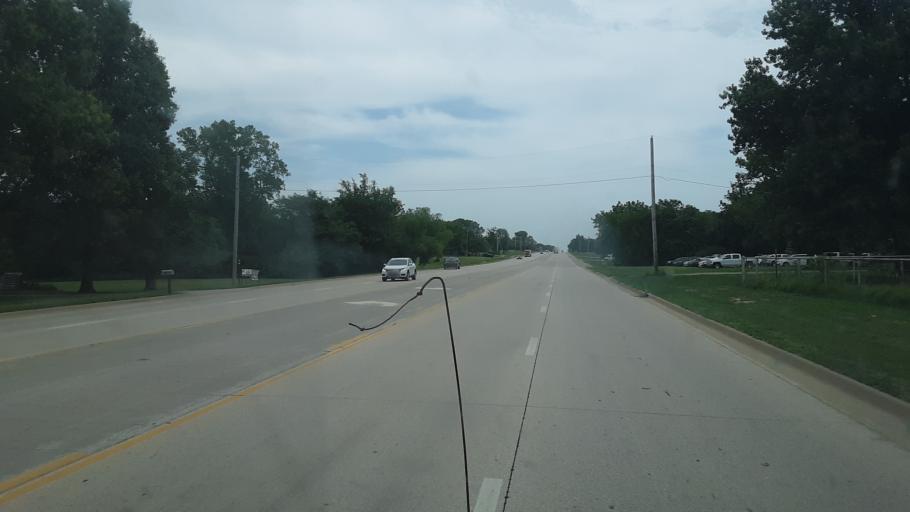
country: US
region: Kansas
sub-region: Allen County
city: Iola
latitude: 37.9220
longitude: -95.3629
